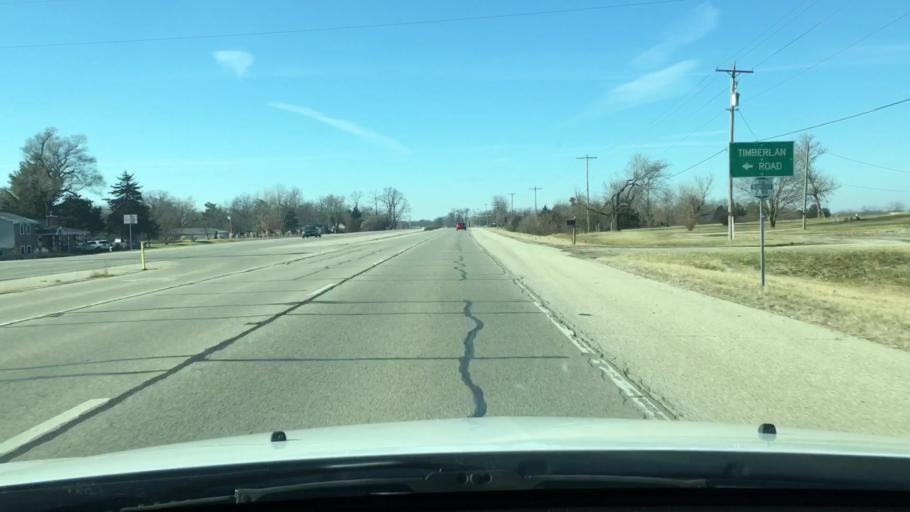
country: US
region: Illinois
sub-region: Woodford County
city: Germantown Hills
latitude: 40.7679
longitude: -89.4598
